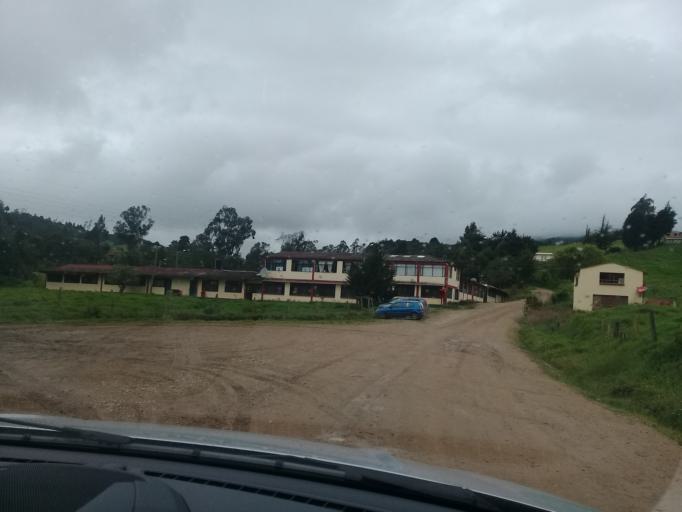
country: CO
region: Boyaca
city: Samaca
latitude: 5.4452
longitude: -73.4371
